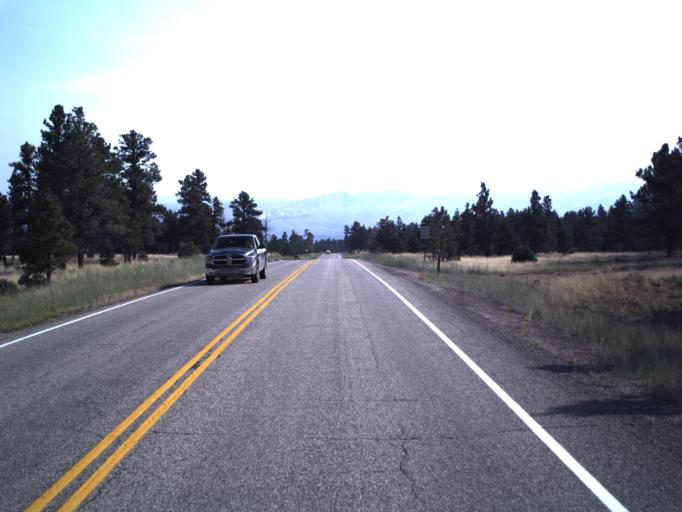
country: US
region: Utah
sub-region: Daggett County
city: Manila
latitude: 40.8757
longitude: -109.4648
